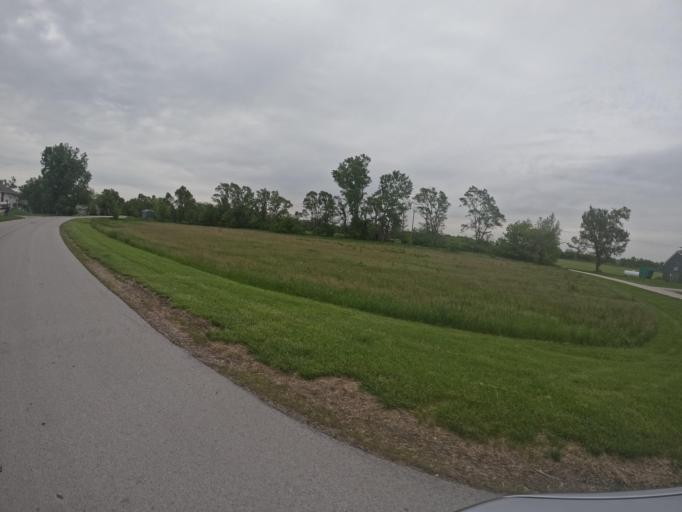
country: US
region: Nebraska
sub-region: Sarpy County
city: Offutt Air Force Base
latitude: 41.0488
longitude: -95.9527
